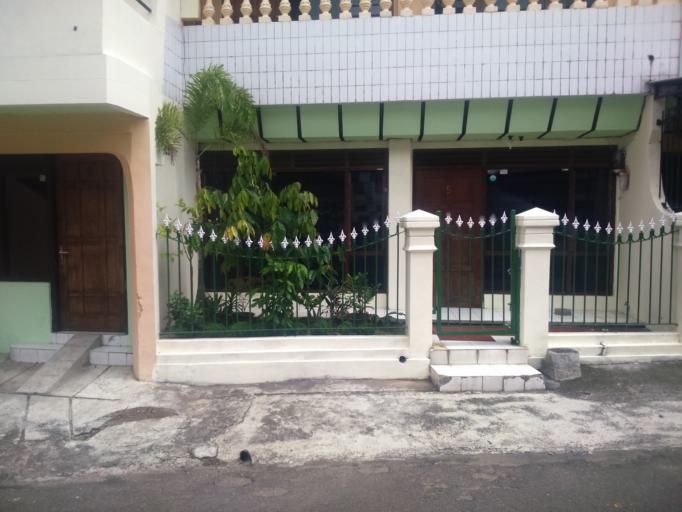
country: ID
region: Daerah Istimewa Yogyakarta
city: Yogyakarta
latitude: -7.8008
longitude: 110.3716
